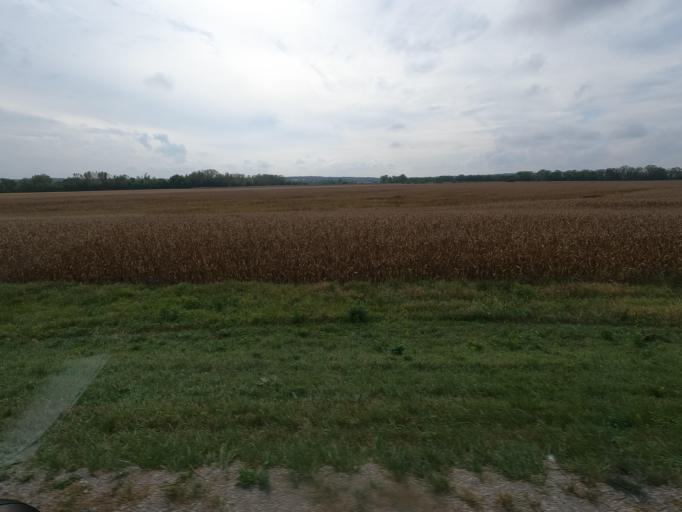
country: US
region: Iowa
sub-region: Jefferson County
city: Fairfield
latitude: 40.8818
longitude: -92.1600
